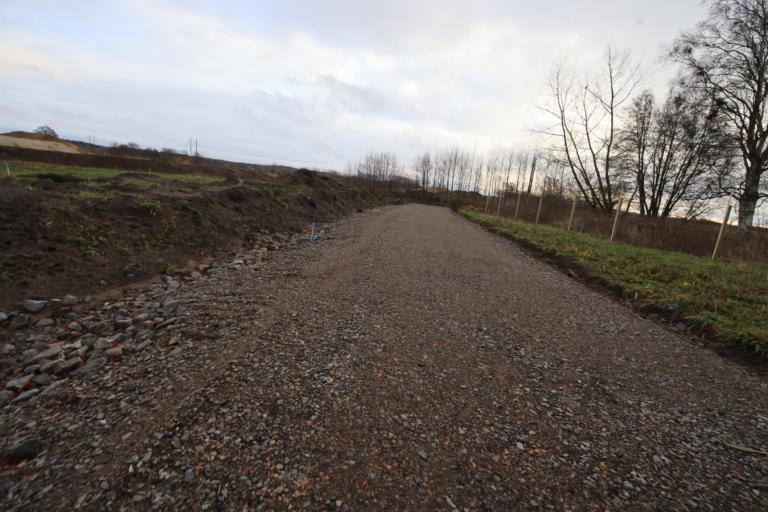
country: SE
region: Halland
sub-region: Varbergs Kommun
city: Traslovslage
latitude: 57.0856
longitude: 12.2906
